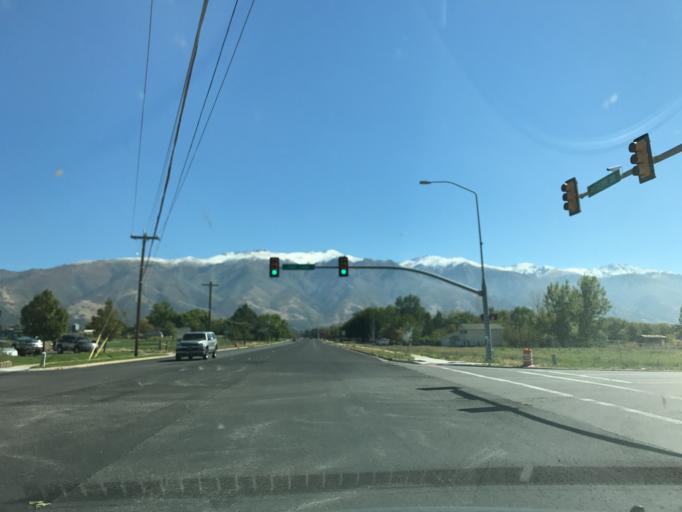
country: US
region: Utah
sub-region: Davis County
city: Hill Air Force Bace
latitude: 41.0891
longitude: -111.9596
